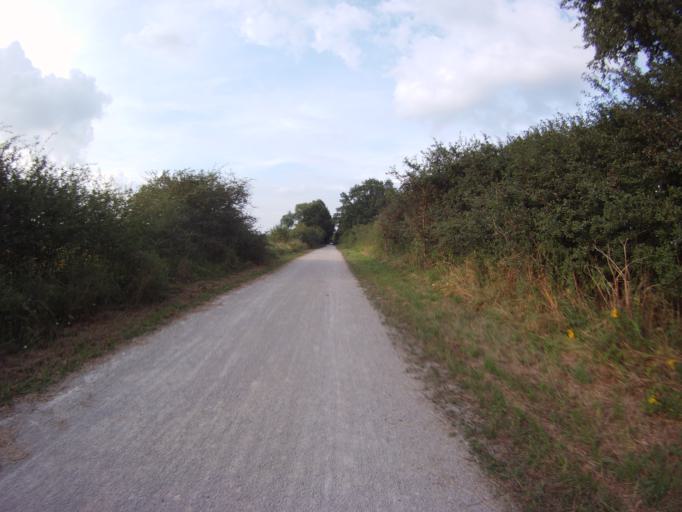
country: FR
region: Lorraine
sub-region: Departement de la Moselle
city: Courcelles-Chaussy
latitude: 49.0938
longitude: 6.3822
